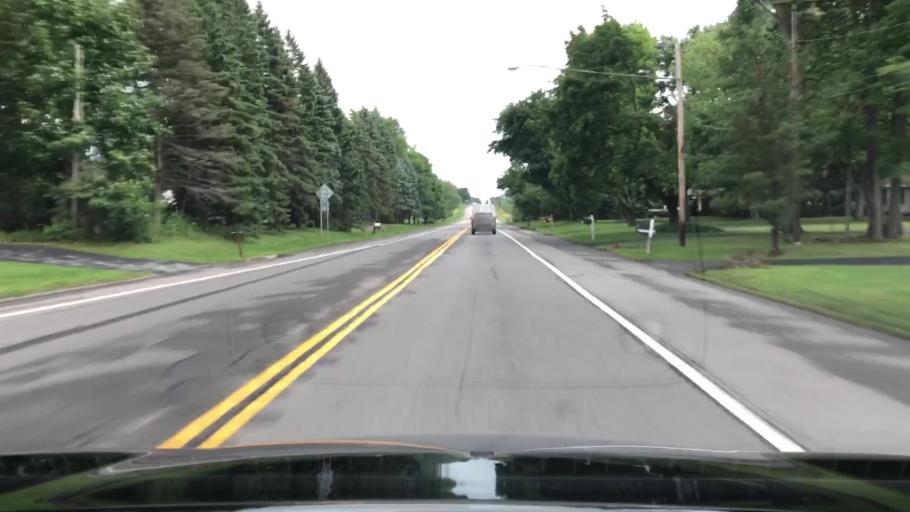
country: US
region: New York
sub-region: Erie County
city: Orchard Park
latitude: 42.8104
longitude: -78.6969
